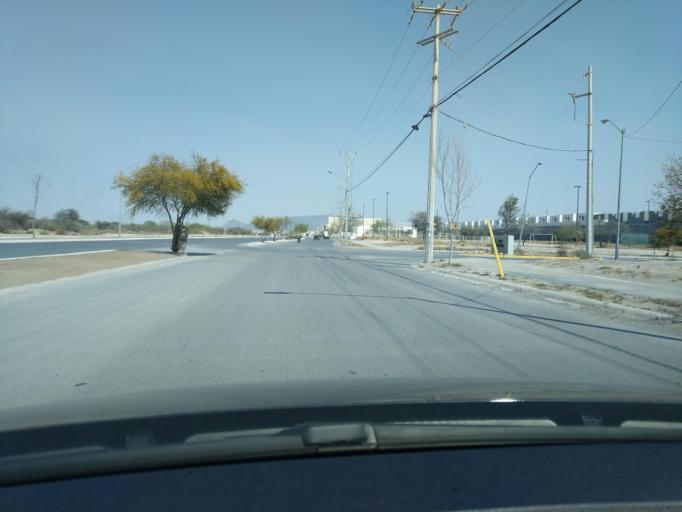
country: MX
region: Nuevo Leon
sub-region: Garcia
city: Los Parques
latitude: 25.7818
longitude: -100.4952
